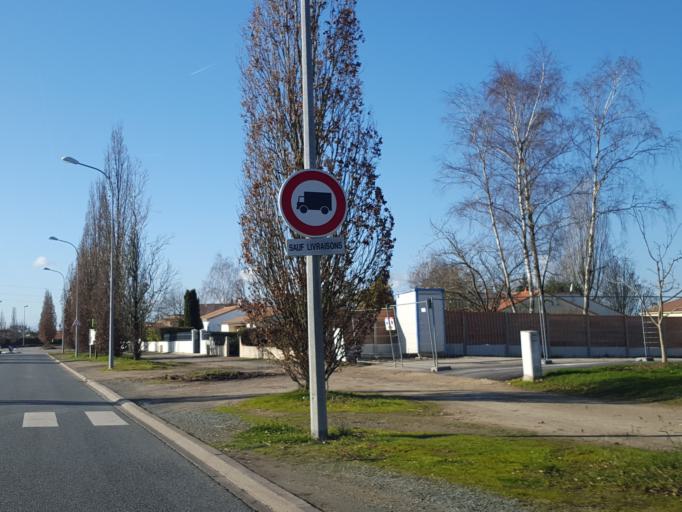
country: FR
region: Pays de la Loire
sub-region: Departement de la Vendee
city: La Roche-sur-Yon
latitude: 46.6583
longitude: -1.4482
